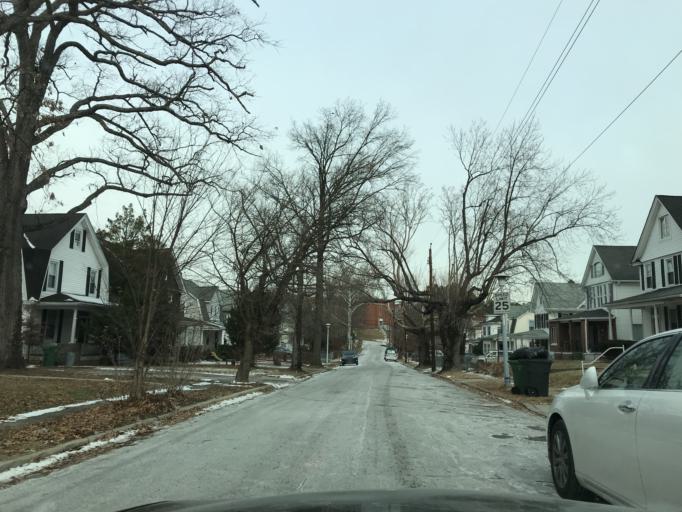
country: US
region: Maryland
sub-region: Baltimore County
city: Towson
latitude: 39.3525
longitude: -76.6014
